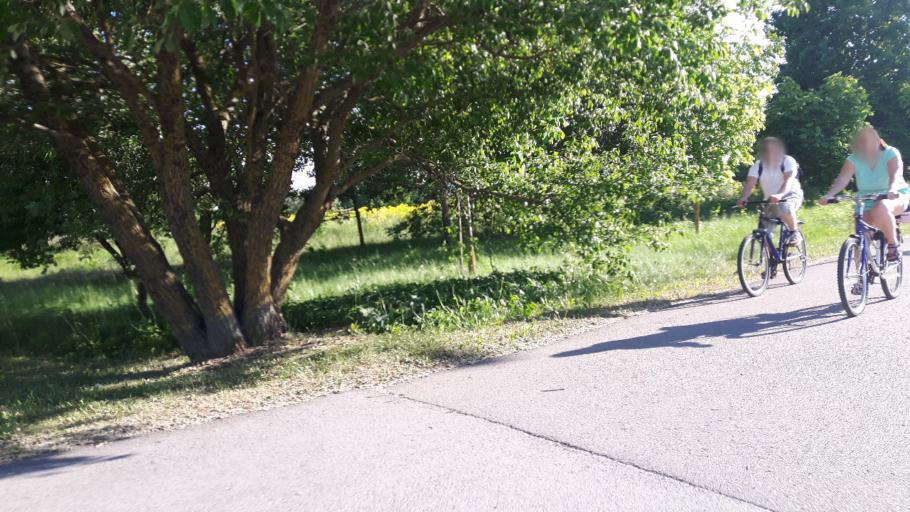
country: EE
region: Harju
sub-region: Tallinna linn
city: Kose
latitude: 59.4513
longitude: 24.8590
